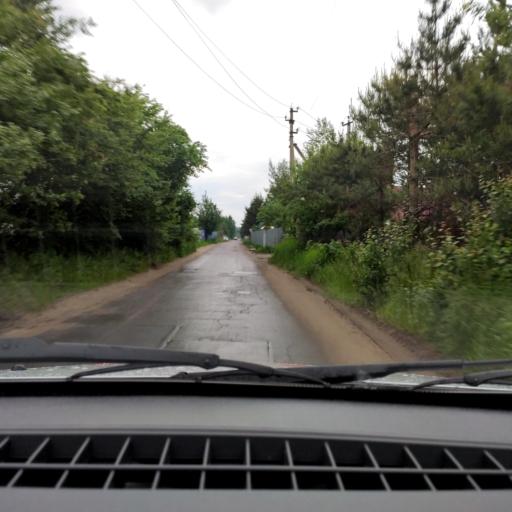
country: RU
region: Voronezj
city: Ramon'
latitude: 51.8537
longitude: 39.2425
